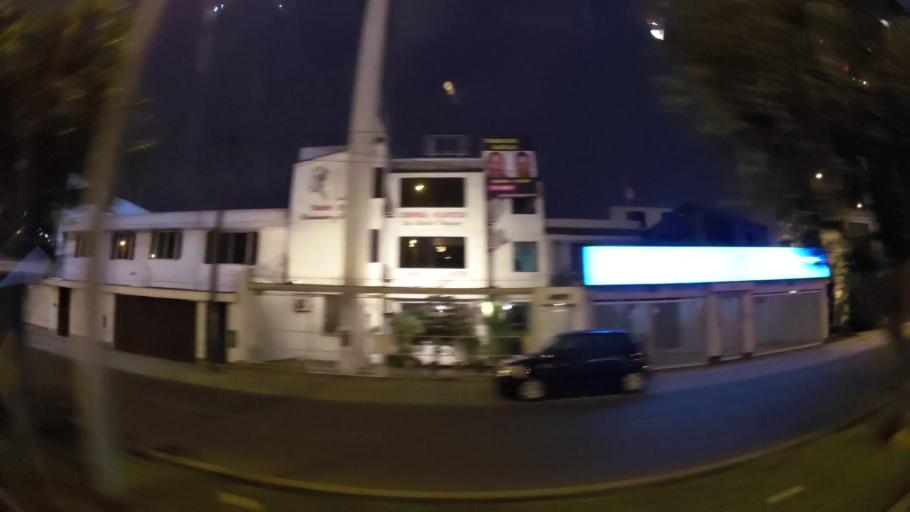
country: PE
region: Lima
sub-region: Lima
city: San Luis
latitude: -12.0843
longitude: -76.9774
